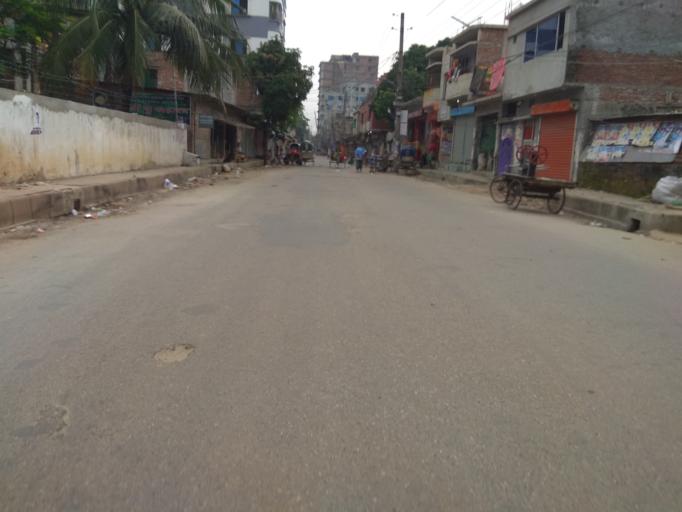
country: BD
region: Dhaka
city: Azimpur
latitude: 23.7127
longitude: 90.3709
